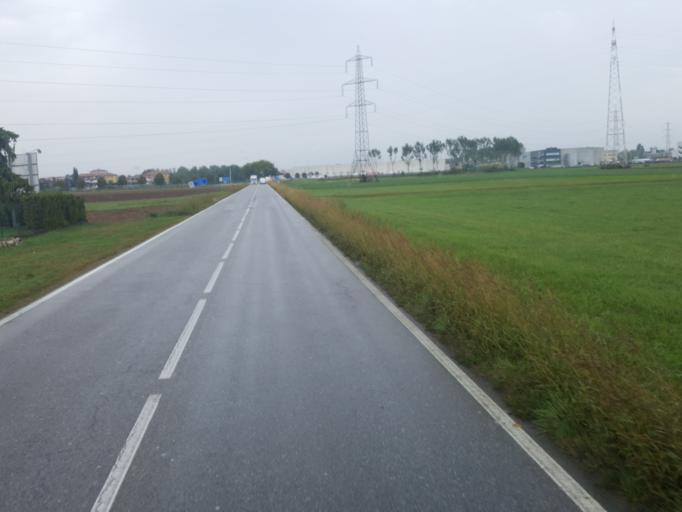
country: IT
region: Lombardy
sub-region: Provincia di Varese
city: Origgio
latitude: 45.5857
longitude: 9.0246
